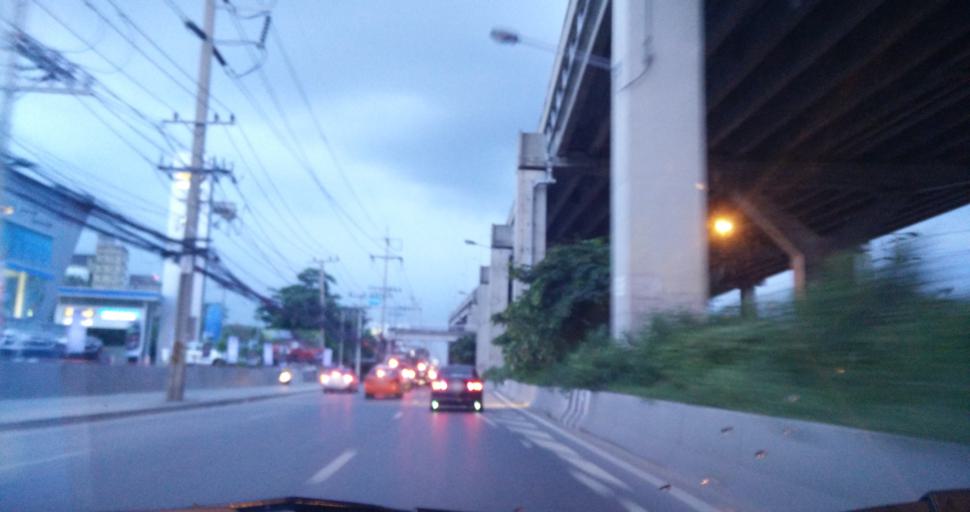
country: TH
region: Phra Nakhon Si Ayutthaya
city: Ban Bang Kadi Pathum Thani
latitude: 13.9993
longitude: 100.6147
